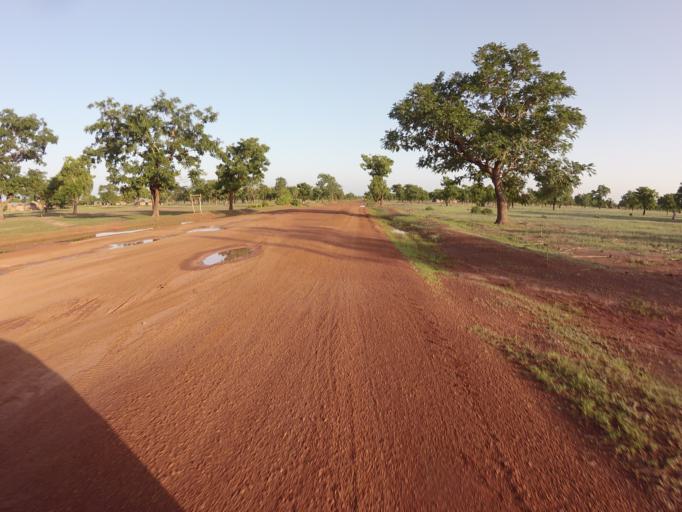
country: TG
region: Savanes
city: Sansanne-Mango
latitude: 10.2786
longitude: -0.0837
